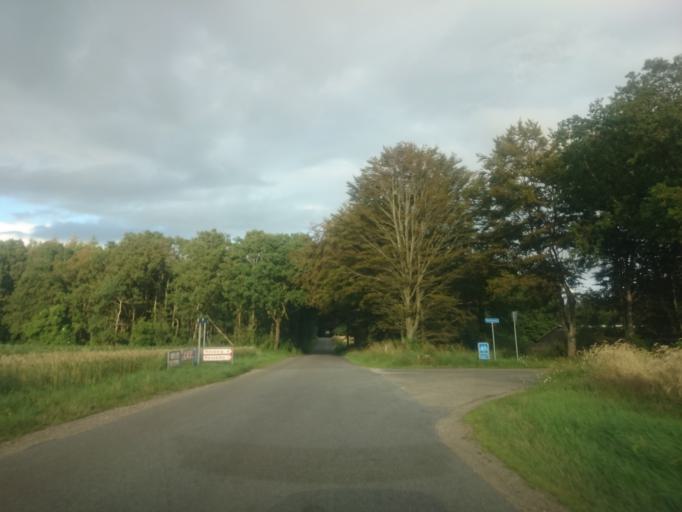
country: DK
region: South Denmark
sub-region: Billund Kommune
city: Grindsted
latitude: 55.6473
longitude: 8.8469
